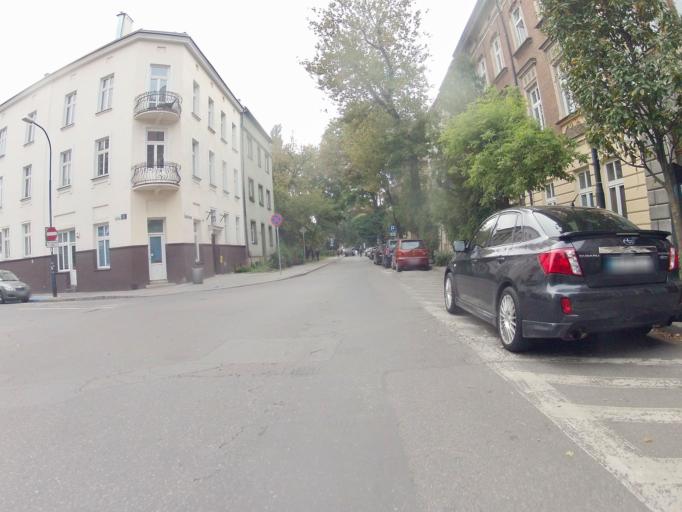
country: PL
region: Lesser Poland Voivodeship
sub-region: Krakow
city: Krakow
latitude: 50.0424
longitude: 19.9414
